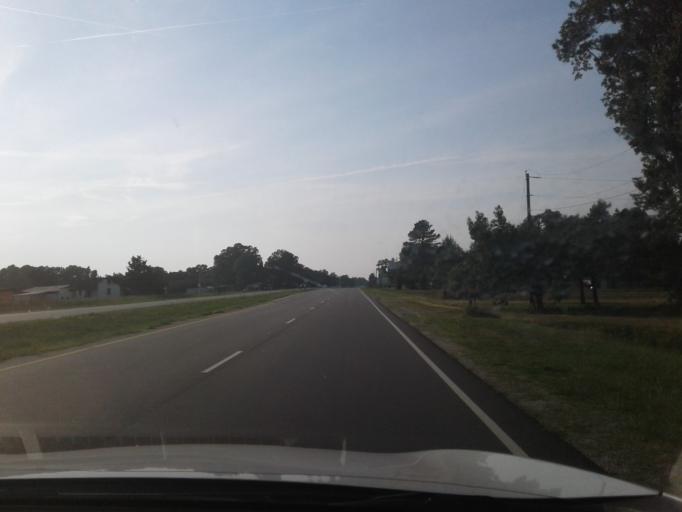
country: US
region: North Carolina
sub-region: Harnett County
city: Erwin
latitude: 35.3538
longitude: -78.6943
